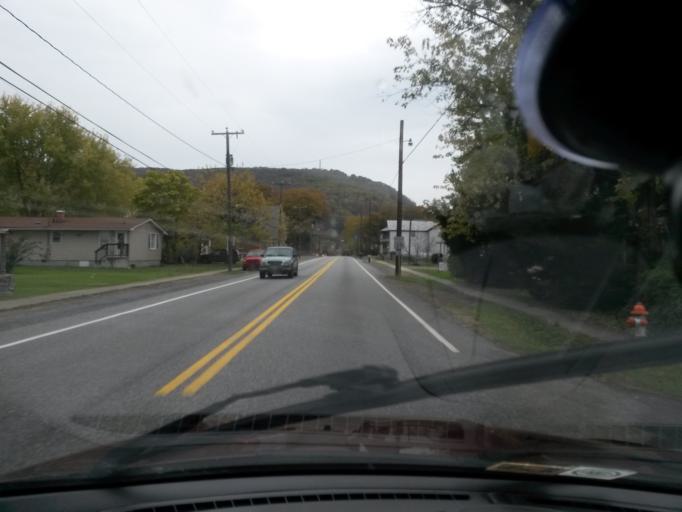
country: US
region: Virginia
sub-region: Alleghany County
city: Clifton Forge
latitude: 37.7951
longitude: -79.7888
